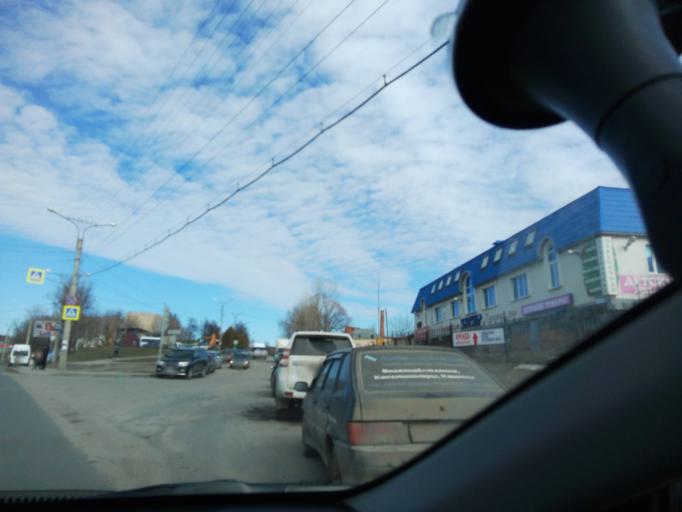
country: RU
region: Chuvashia
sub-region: Cheboksarskiy Rayon
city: Cheboksary
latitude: 56.1138
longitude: 47.2508
